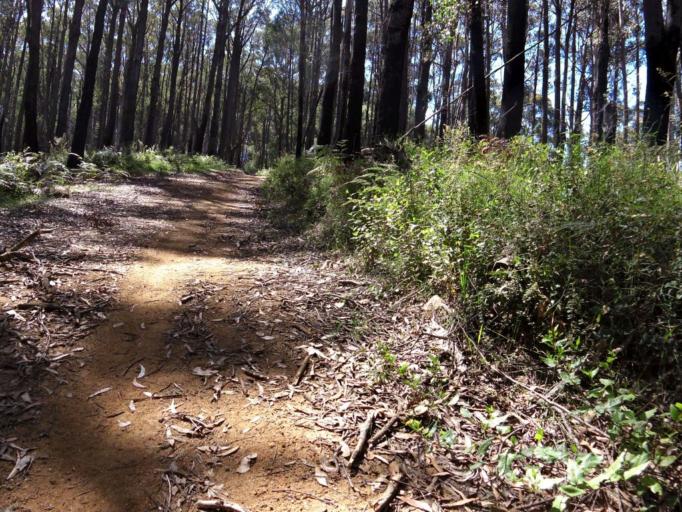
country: AU
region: Victoria
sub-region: Yarra Ranges
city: Millgrove
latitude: -37.8593
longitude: 145.7521
